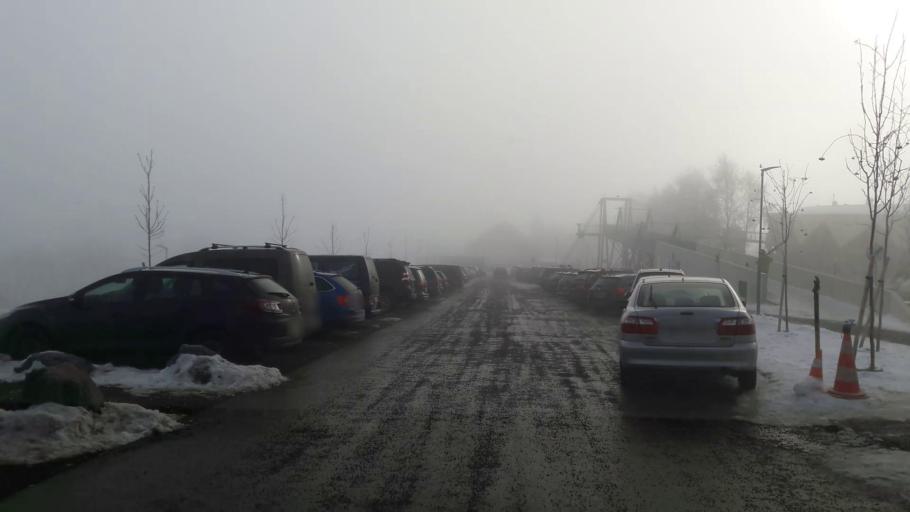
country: AT
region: Lower Austria
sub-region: Politischer Bezirk Neunkirchen
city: Sankt Corona am Wechsel
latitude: 47.5786
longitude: 16.0202
